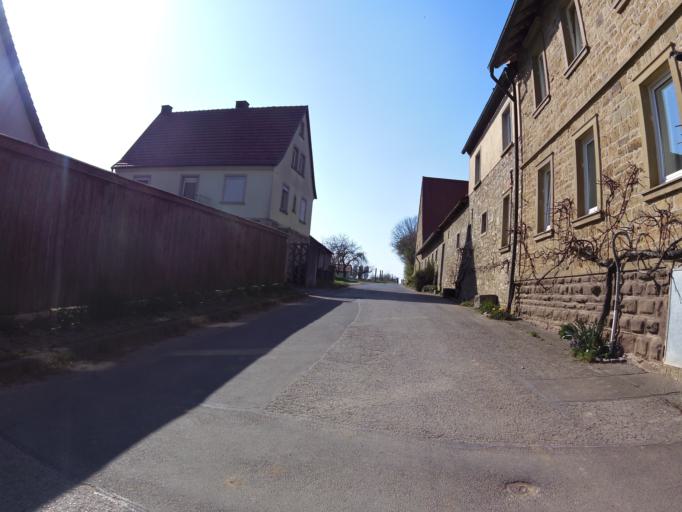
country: DE
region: Bavaria
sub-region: Regierungsbezirk Unterfranken
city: Prosselsheim
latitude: 49.8247
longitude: 10.1062
